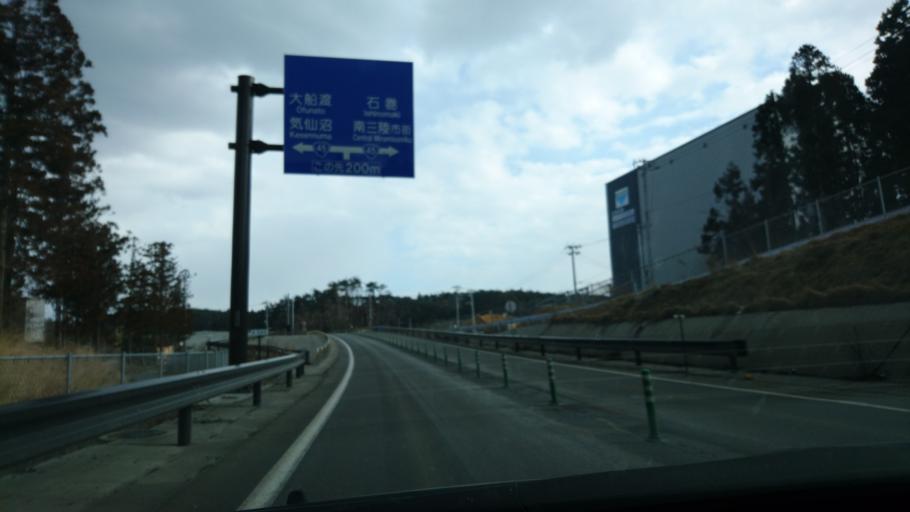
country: JP
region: Miyagi
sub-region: Oshika Gun
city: Onagawa Cho
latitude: 38.6922
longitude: 141.4639
